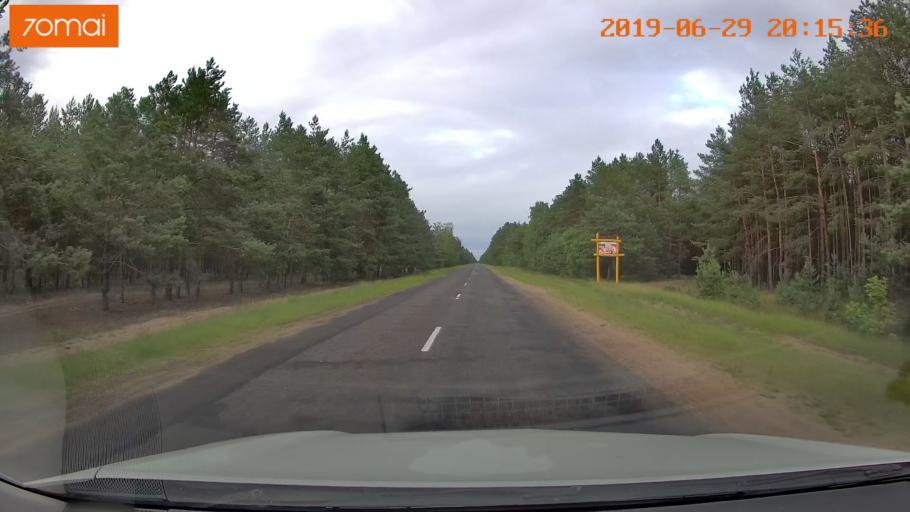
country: BY
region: Brest
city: Asnyezhytsy
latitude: 52.3754
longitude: 26.1791
